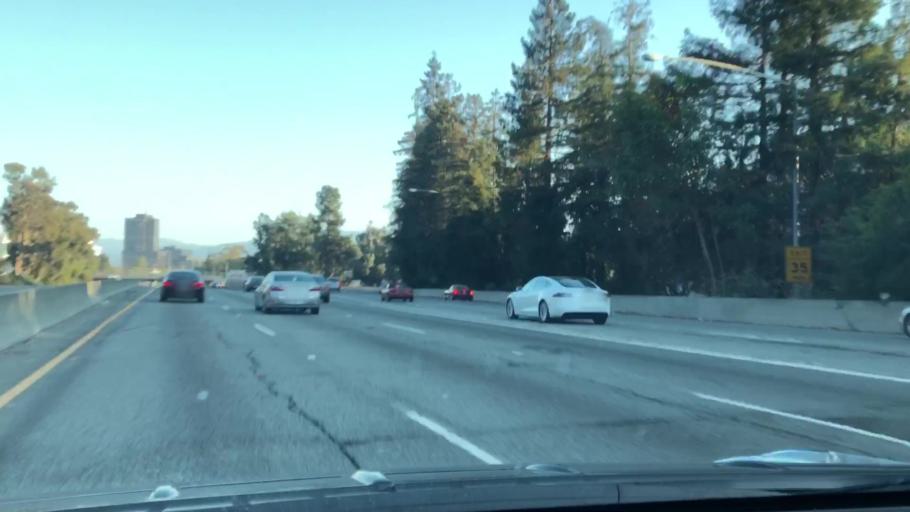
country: US
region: California
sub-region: Santa Clara County
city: Campbell
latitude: 37.2969
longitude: -121.9400
